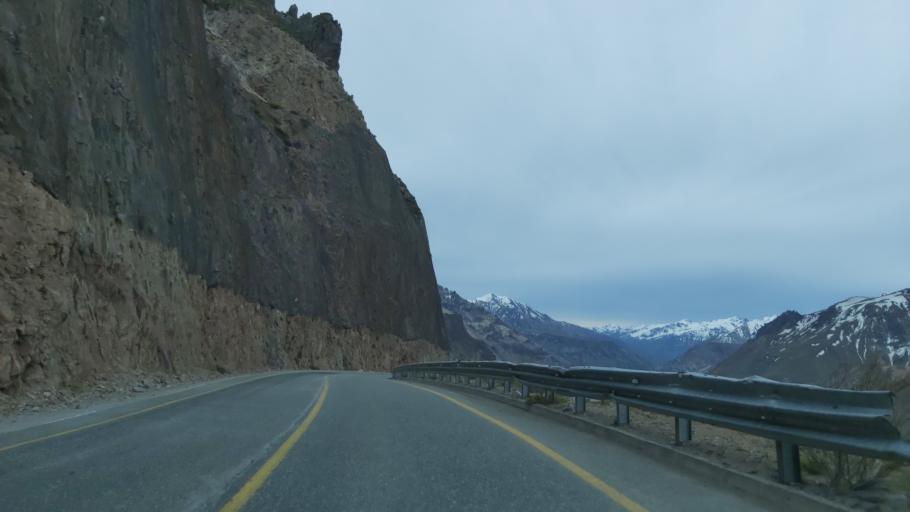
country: CL
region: Maule
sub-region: Provincia de Linares
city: Colbun
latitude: -35.9559
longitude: -70.5793
